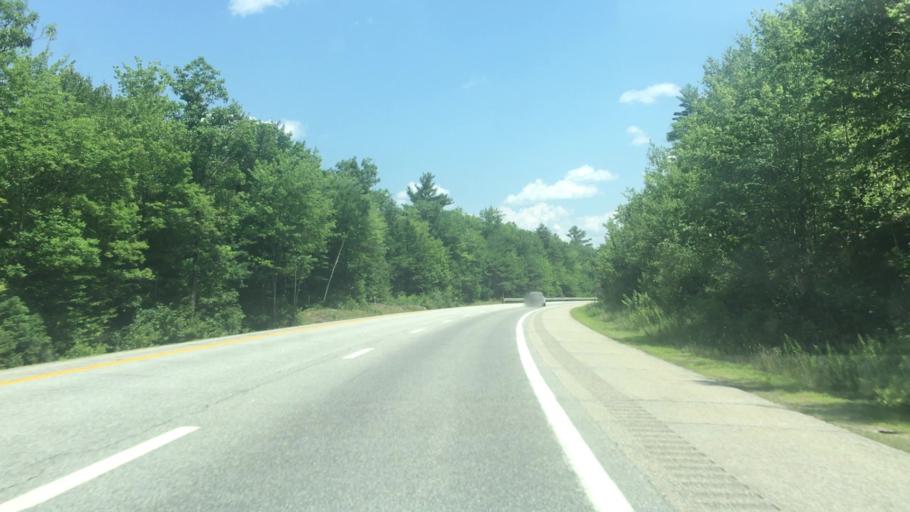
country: US
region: New Hampshire
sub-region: Merrimack County
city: Sutton
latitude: 43.3181
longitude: -71.8734
